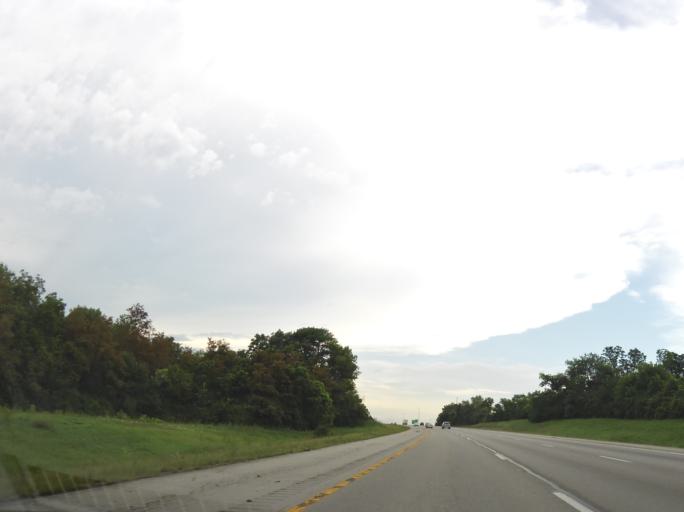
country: US
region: Kentucky
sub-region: Madison County
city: Richmond
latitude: 37.6640
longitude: -84.3099
